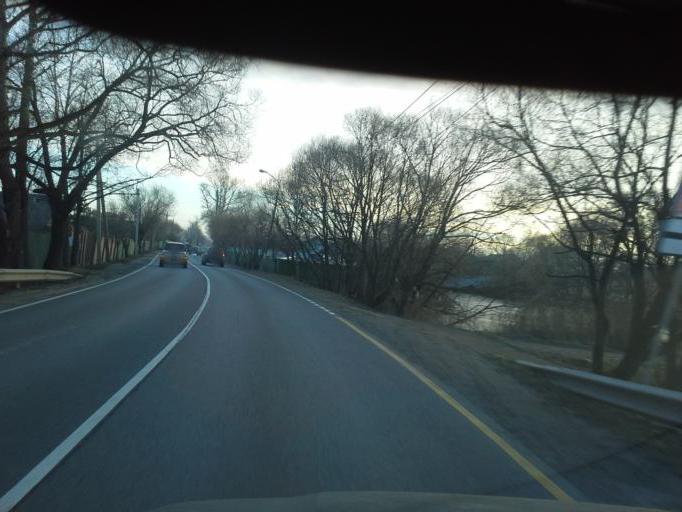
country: RU
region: Moskovskaya
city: Kokoshkino
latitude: 55.5945
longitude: 37.1154
